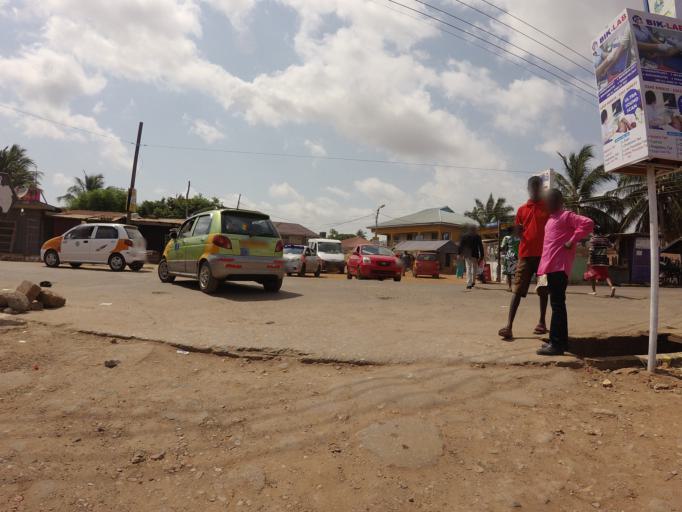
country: GH
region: Greater Accra
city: Dome
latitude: 5.6184
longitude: -0.2499
